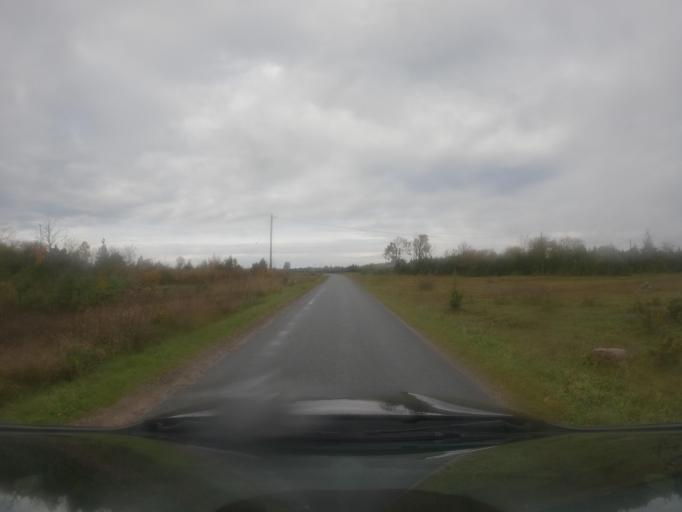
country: EE
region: Saare
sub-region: Kuressaare linn
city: Kuressaare
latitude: 58.4433
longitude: 21.9832
